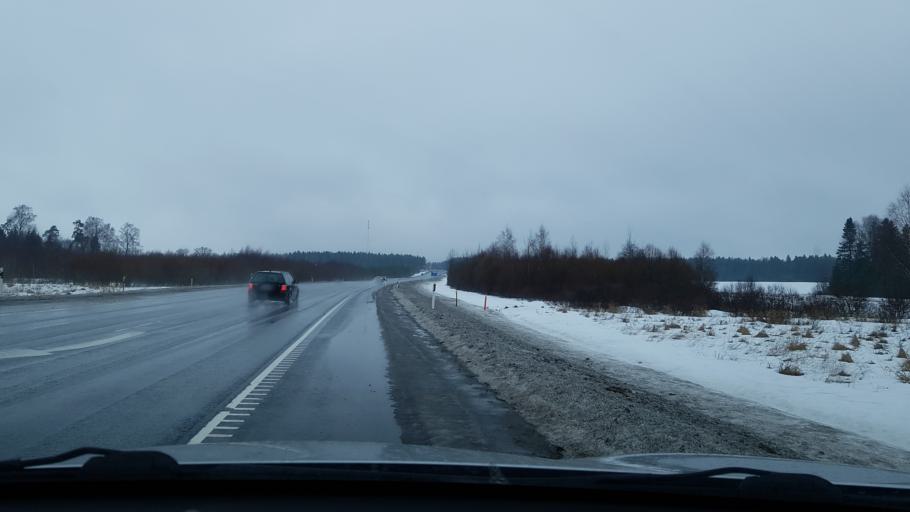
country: EE
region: Raplamaa
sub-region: Kohila vald
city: Kohila
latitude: 59.1748
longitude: 24.7749
